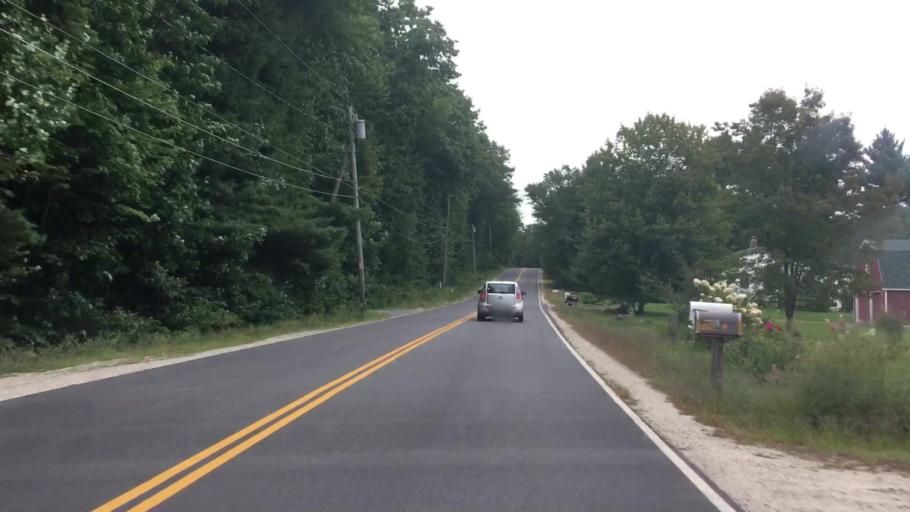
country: US
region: Maine
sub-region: Cumberland County
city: New Gloucester
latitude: 43.8882
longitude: -70.2530
